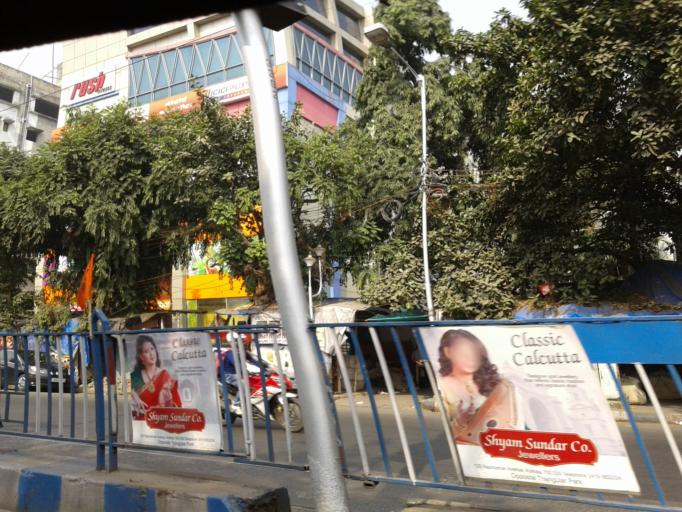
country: IN
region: West Bengal
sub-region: Kolkata
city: Kolkata
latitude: 22.5190
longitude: 88.3618
